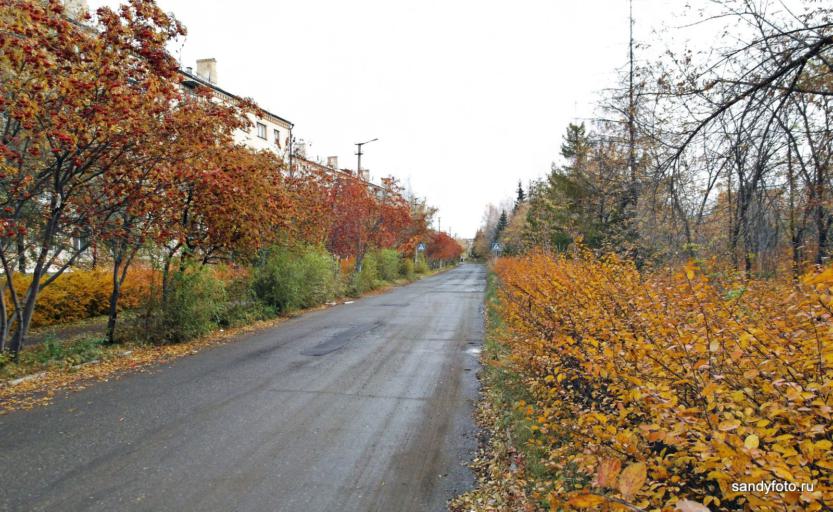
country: RU
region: Chelyabinsk
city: Troitsk
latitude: 54.0475
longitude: 61.6315
